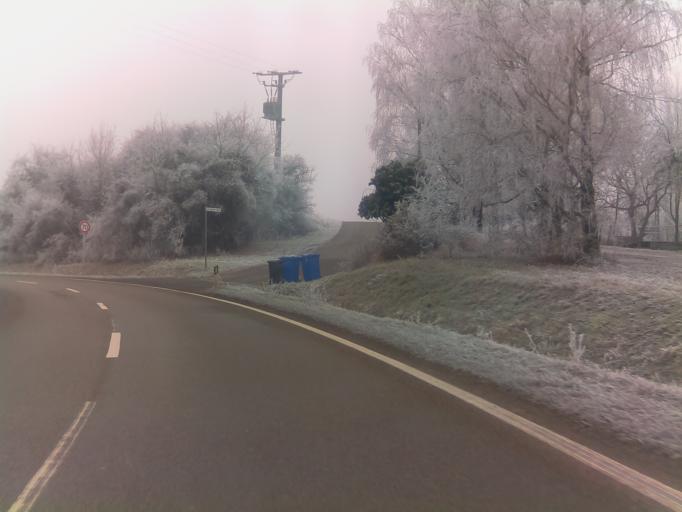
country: DE
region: Bavaria
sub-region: Regierungsbezirk Unterfranken
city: Hassfurt
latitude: 50.0773
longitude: 10.5618
